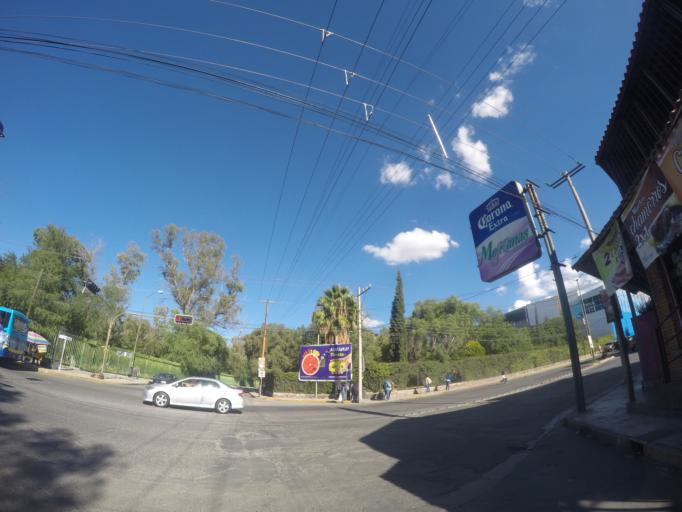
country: MX
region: San Luis Potosi
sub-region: San Luis Potosi
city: San Luis Potosi
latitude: 22.1509
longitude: -101.0197
